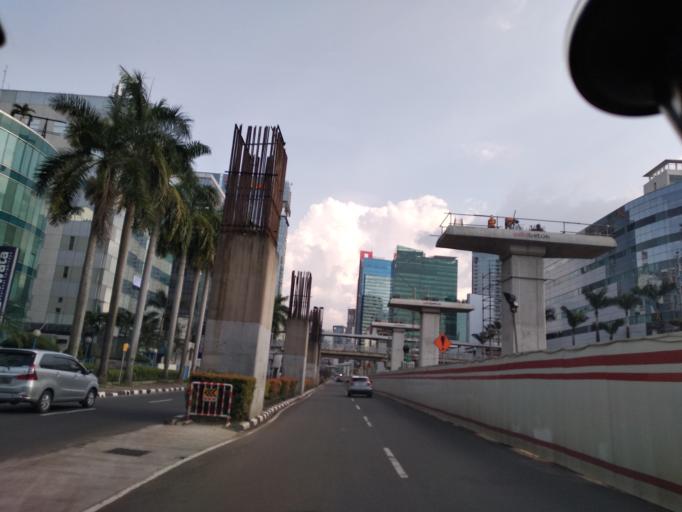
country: ID
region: Jakarta Raya
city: Jakarta
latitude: -6.2132
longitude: 106.8306
